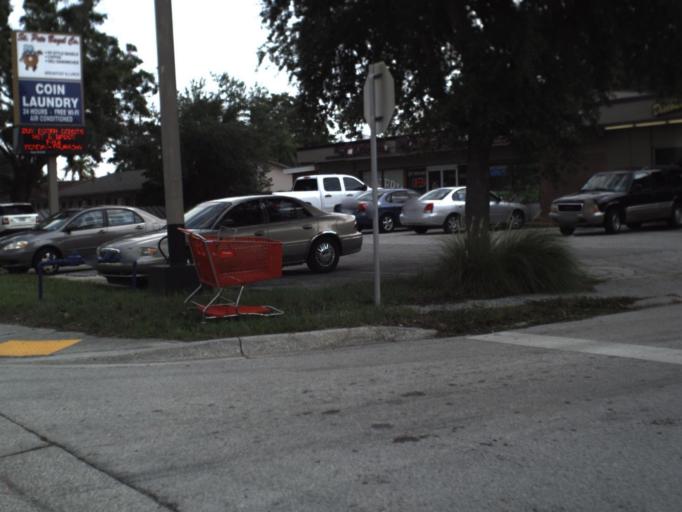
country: US
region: Florida
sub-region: Pinellas County
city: Gandy
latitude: 27.8362
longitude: -82.6386
